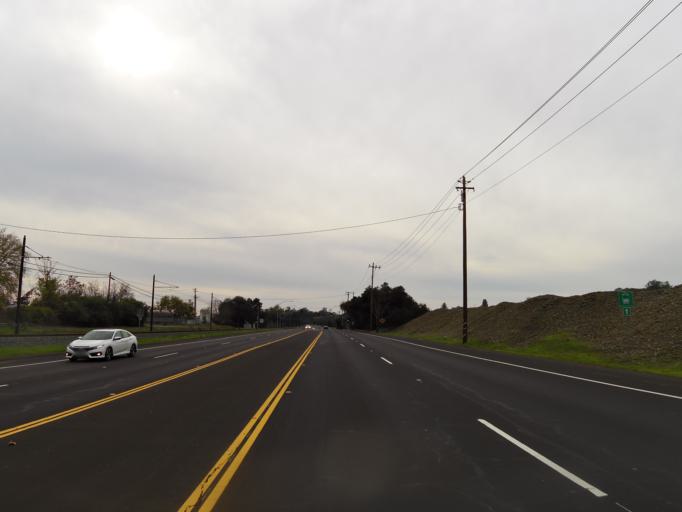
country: US
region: California
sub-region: Sacramento County
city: Folsom
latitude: 38.6701
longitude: -121.1823
